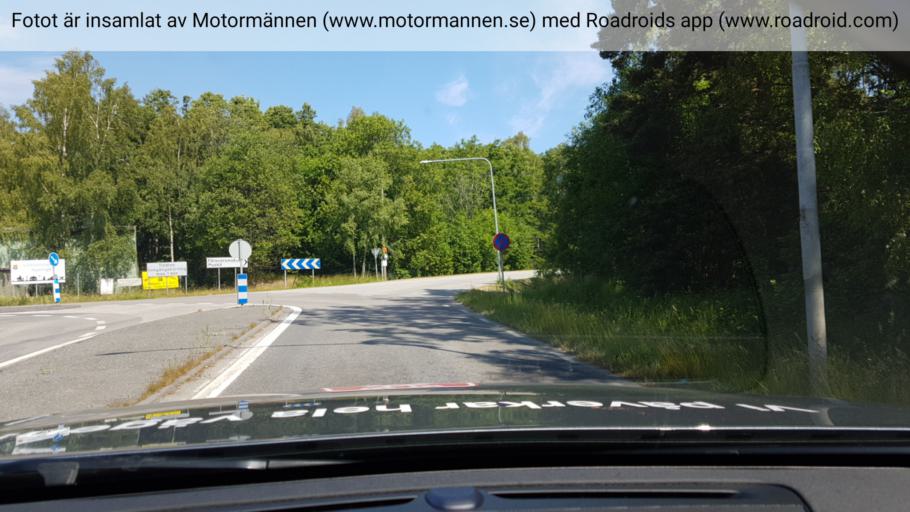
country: SE
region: Stockholm
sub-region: Nynashamns Kommun
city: Nynashamn
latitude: 58.9718
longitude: 18.0619
